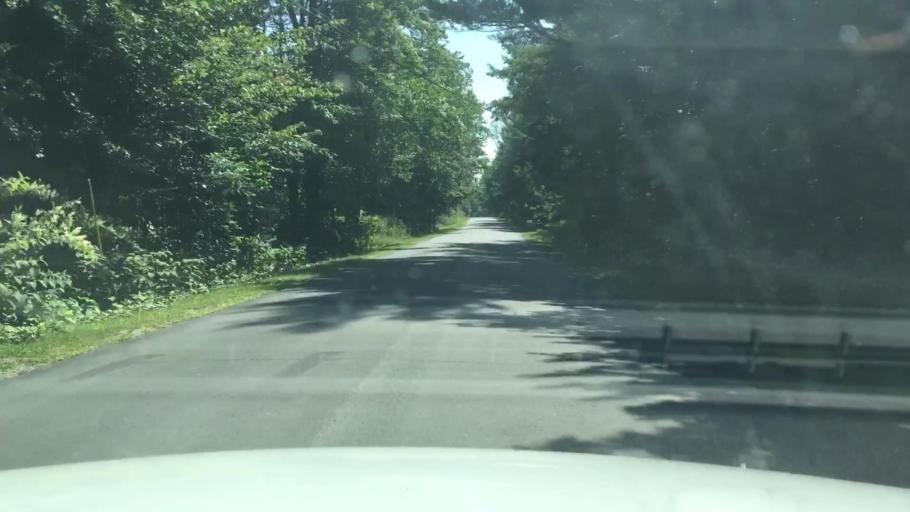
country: US
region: Maine
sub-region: Kennebec County
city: Monmouth
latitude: 44.2631
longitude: -70.0539
